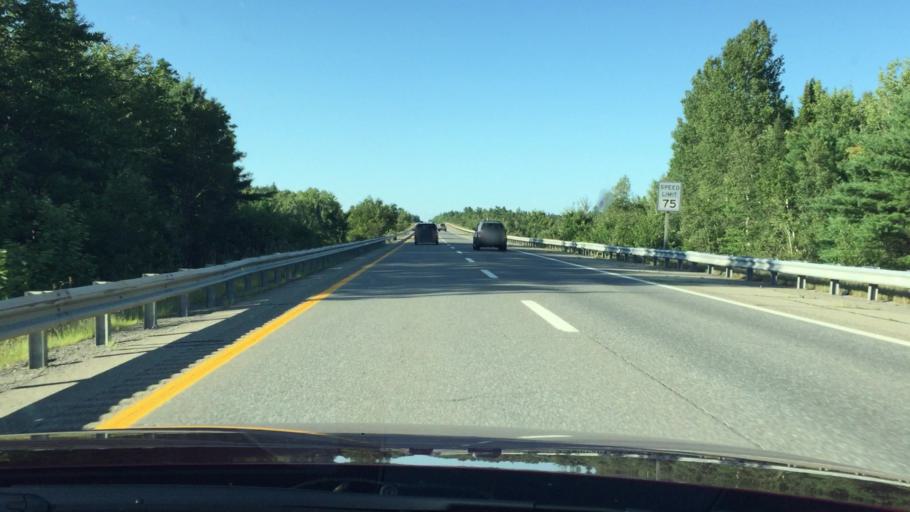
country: US
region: Maine
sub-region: Penobscot County
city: Lincoln
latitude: 45.3911
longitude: -68.6022
